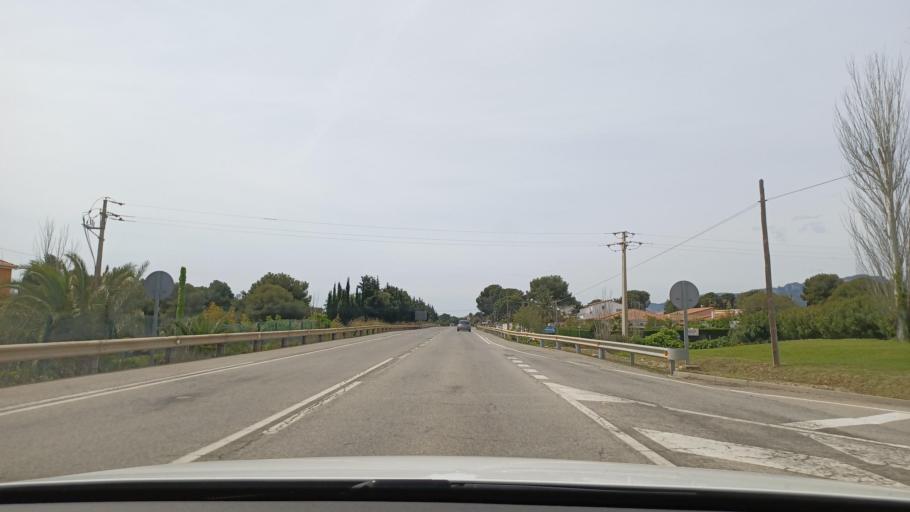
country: ES
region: Catalonia
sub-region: Provincia de Tarragona
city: Vilanova d'Escornalbou
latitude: 41.0342
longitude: 0.9689
